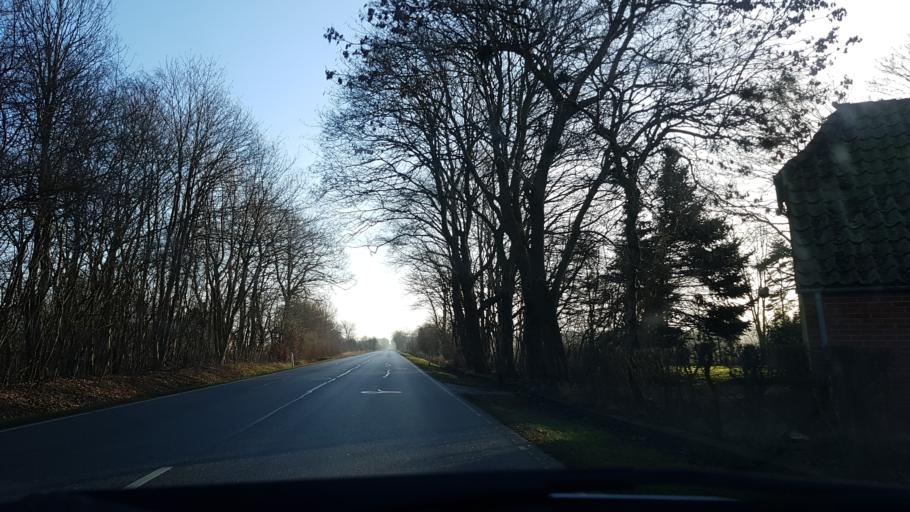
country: DK
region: South Denmark
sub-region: Tonder Kommune
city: Toftlund
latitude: 55.2350
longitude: 9.1648
